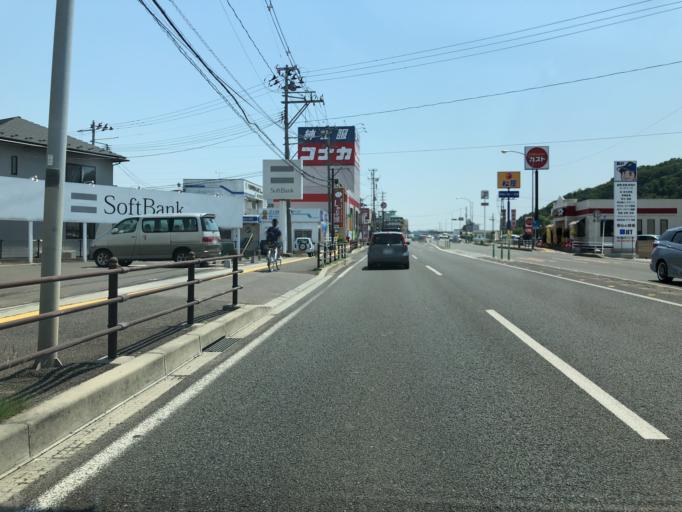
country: JP
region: Fukushima
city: Fukushima-shi
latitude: 37.7802
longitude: 140.4861
